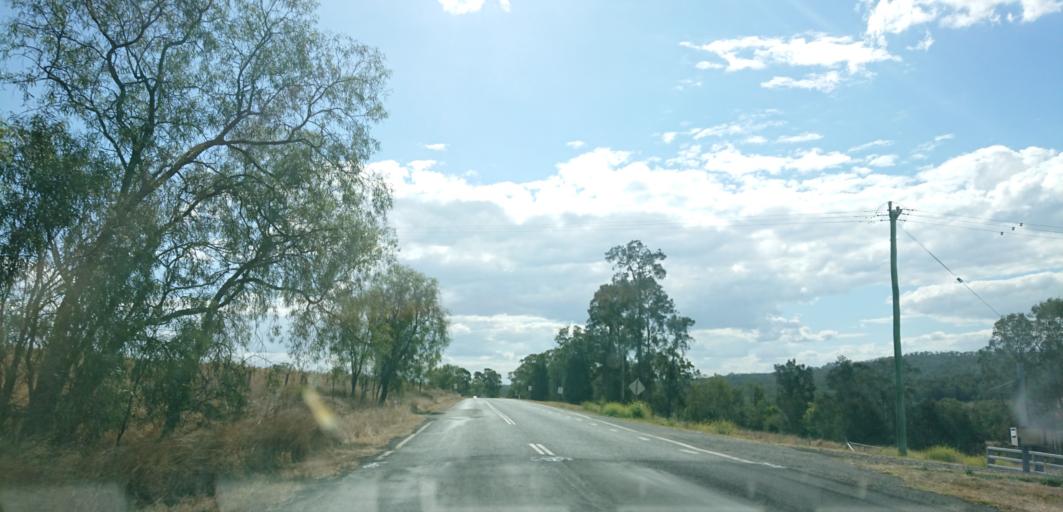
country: AU
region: Queensland
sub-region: Toowoomba
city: Top Camp
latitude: -27.7890
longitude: 152.1002
